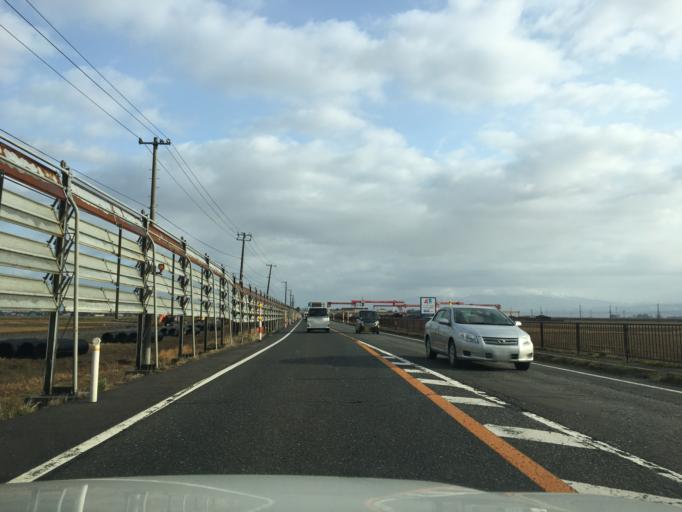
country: JP
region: Yamagata
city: Sakata
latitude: 38.8358
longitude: 139.8479
